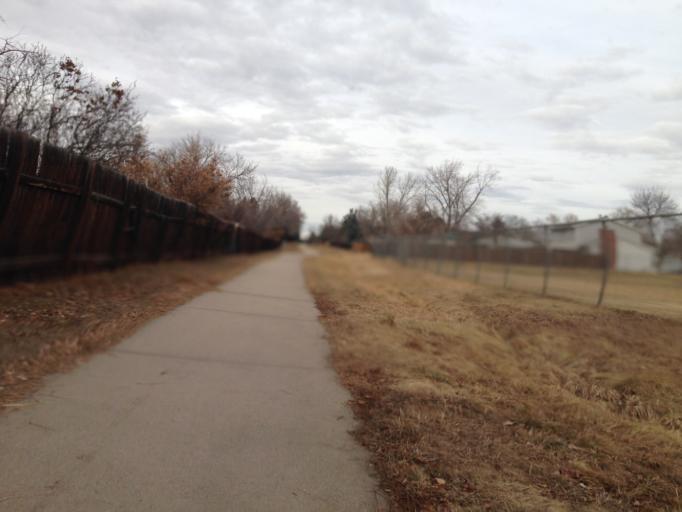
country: US
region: Colorado
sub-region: Adams County
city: Westminster
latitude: 39.8490
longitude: -105.0627
